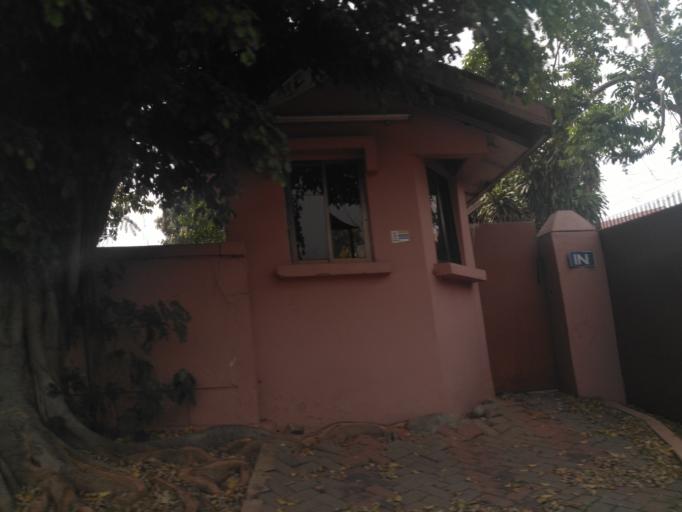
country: GH
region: Ashanti
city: Kumasi
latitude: 6.6732
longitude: -1.6178
